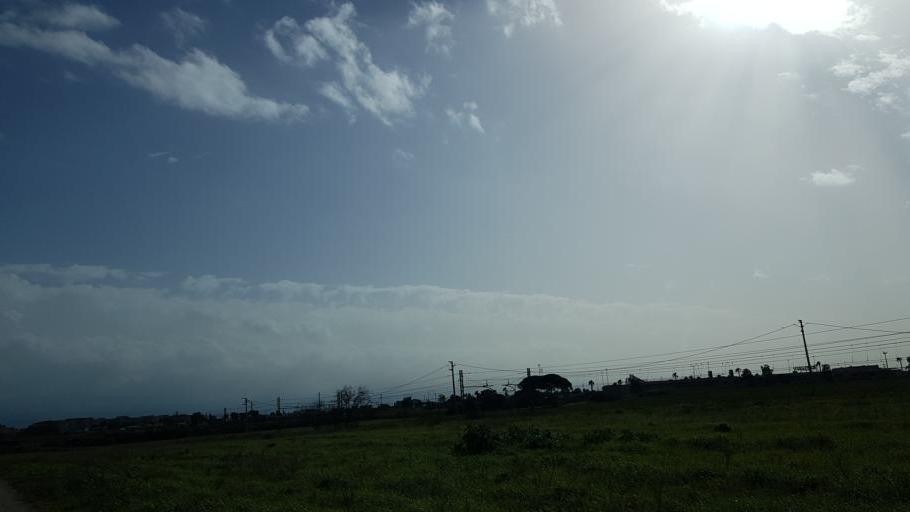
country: IT
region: Apulia
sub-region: Provincia di Brindisi
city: Brindisi
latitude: 40.6239
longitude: 17.8990
